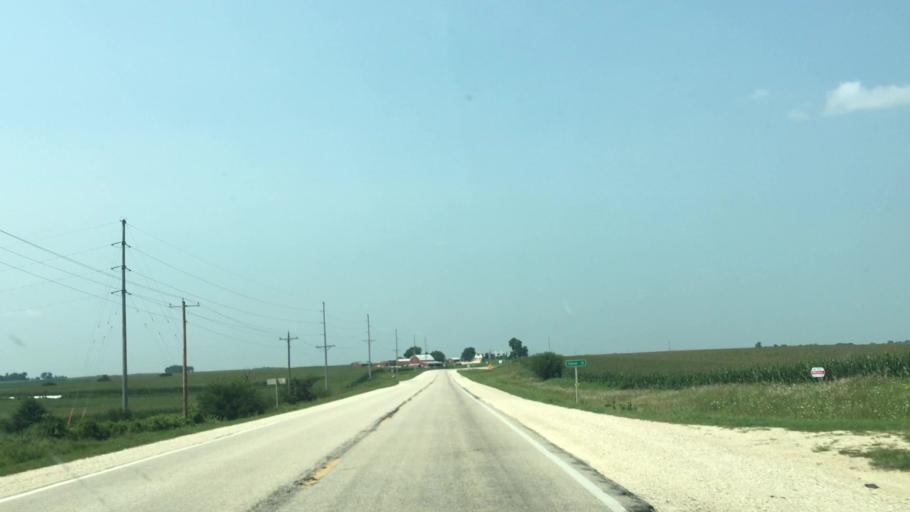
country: US
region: Iowa
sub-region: Fayette County
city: West Union
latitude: 42.9748
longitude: -91.8202
